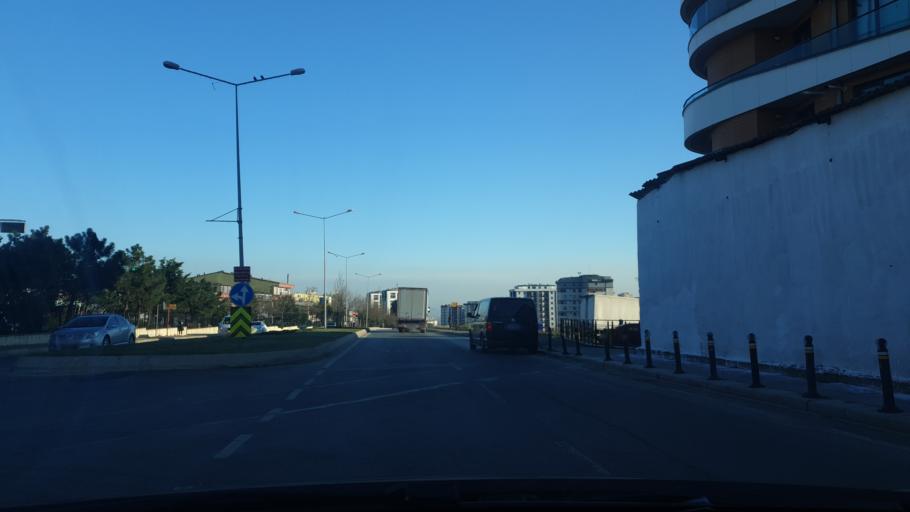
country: TR
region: Istanbul
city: Pendik
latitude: 40.8962
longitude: 29.2605
